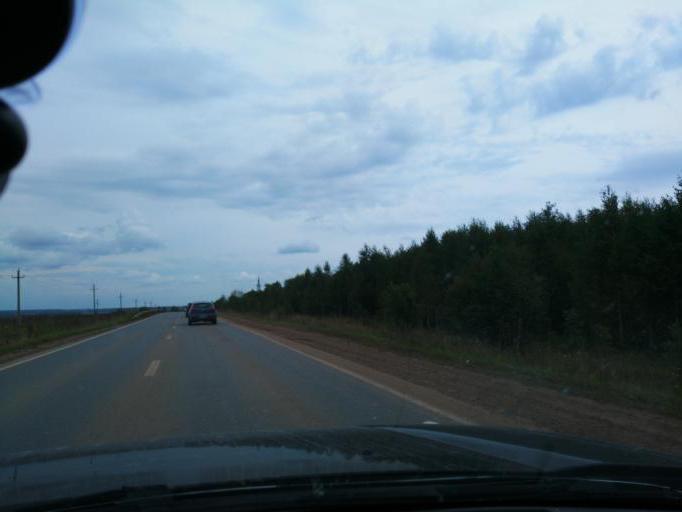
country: RU
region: Perm
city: Chernushka
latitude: 56.5101
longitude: 55.9530
